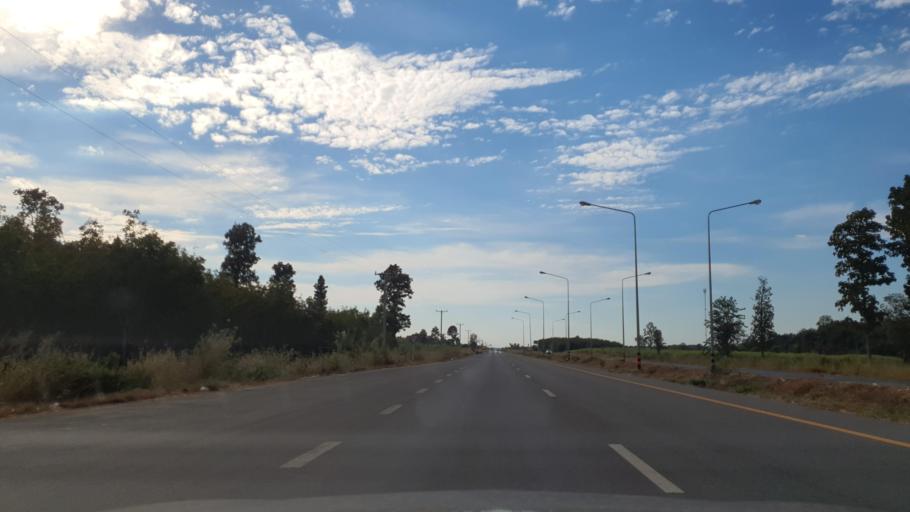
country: TH
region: Roi Et
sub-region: Amphoe Pho Chai
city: Pho Chai
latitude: 16.4151
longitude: 103.8093
